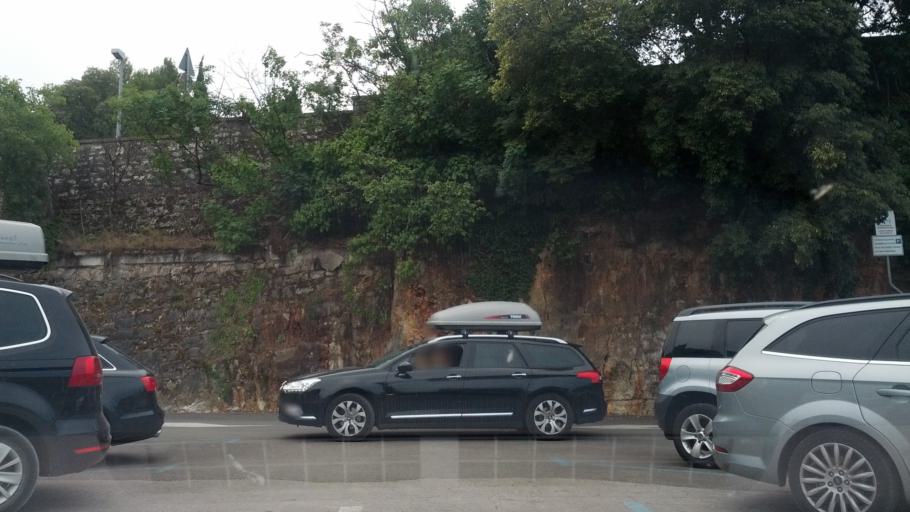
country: HR
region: Istarska
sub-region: Grad Rovinj
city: Rovinj
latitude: 45.0848
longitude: 13.6391
